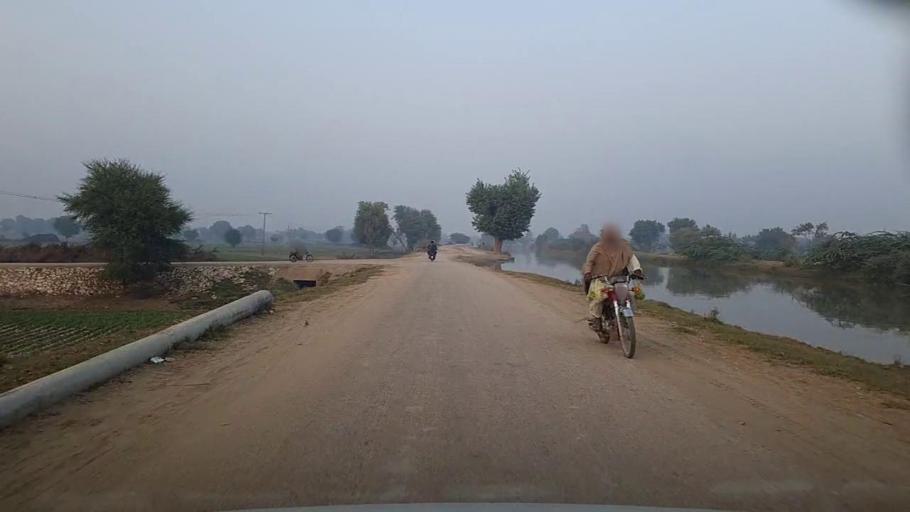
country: PK
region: Sindh
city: Bozdar
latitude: 27.0557
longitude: 68.5991
